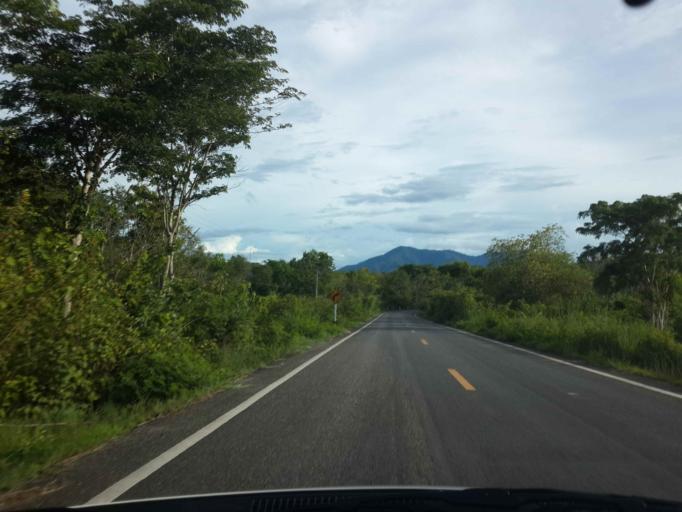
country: TH
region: Kanchanaburi
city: Dan Makham Tia
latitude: 13.8531
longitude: 99.1675
